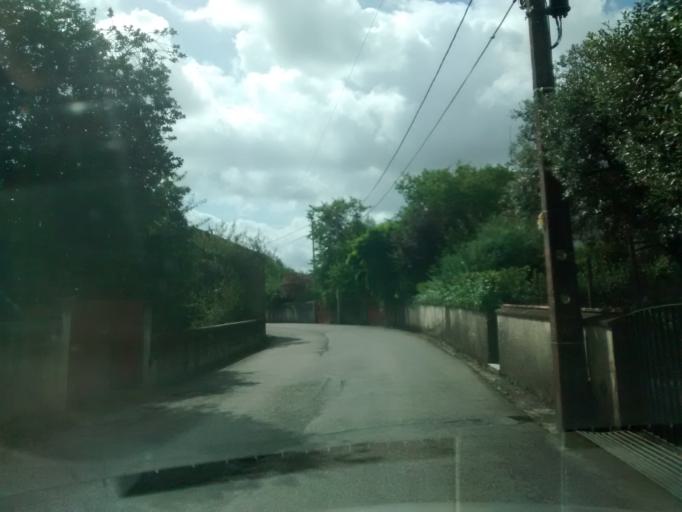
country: PT
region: Aveiro
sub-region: Anadia
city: Sangalhos
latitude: 40.4827
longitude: -8.4891
